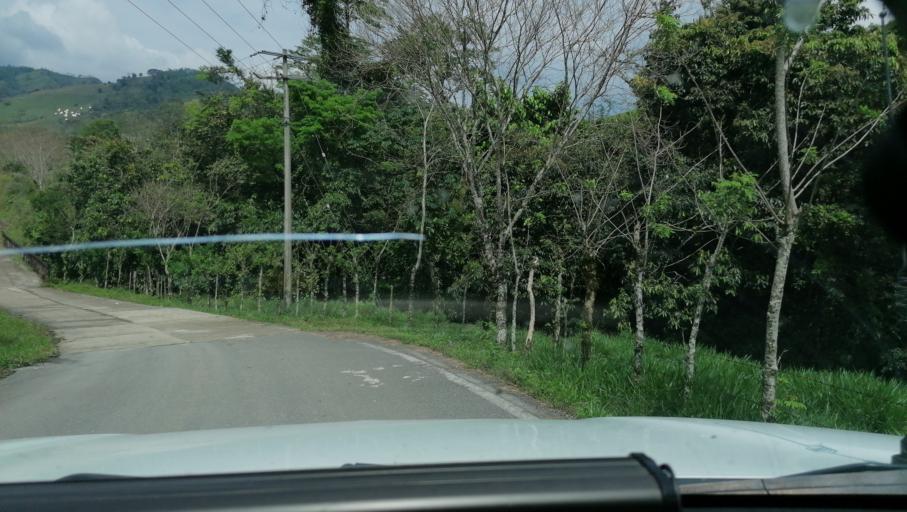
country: MX
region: Chiapas
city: Ocotepec
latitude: 17.3155
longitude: -93.1697
